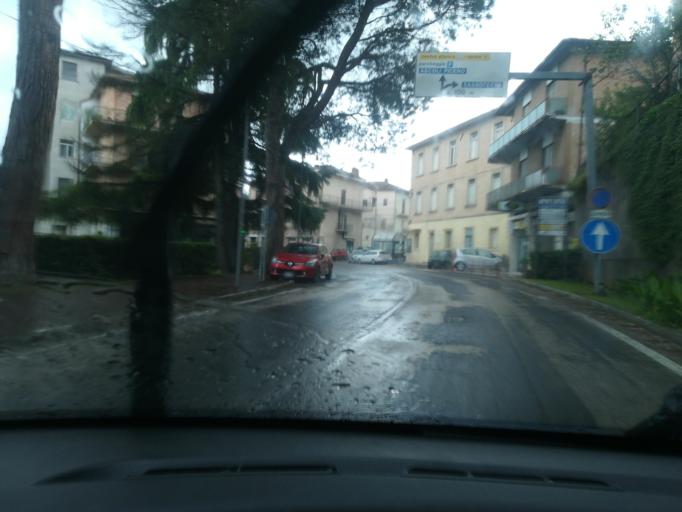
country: IT
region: The Marches
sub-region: Provincia di Macerata
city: Sarnano
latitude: 43.0366
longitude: 13.2979
